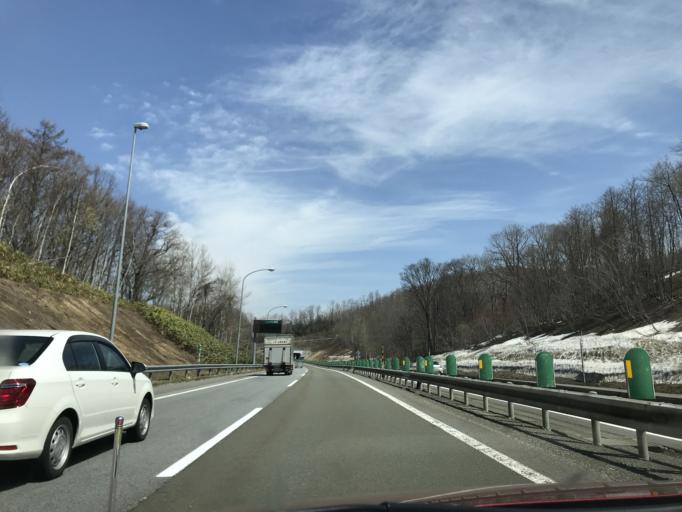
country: JP
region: Hokkaido
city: Bibai
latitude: 43.2853
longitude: 141.8597
